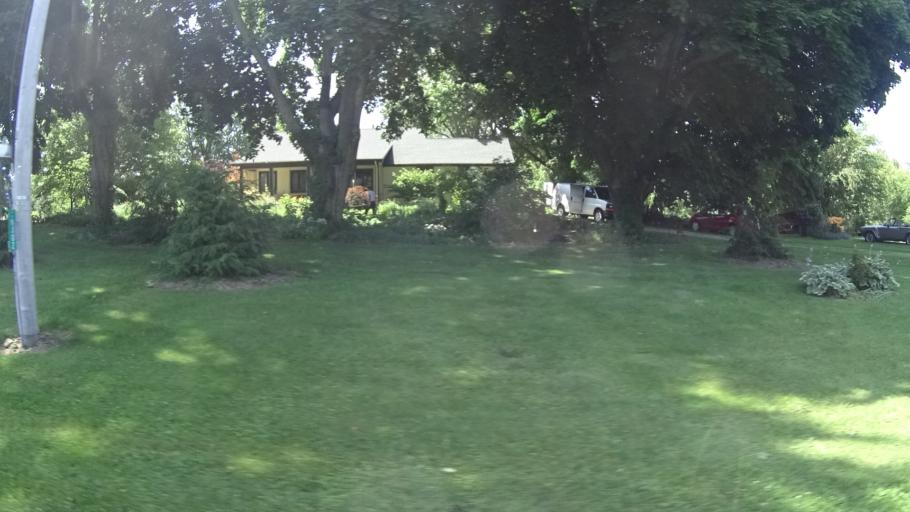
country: US
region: Ohio
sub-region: Lorain County
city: Vermilion
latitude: 41.3545
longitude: -82.4430
